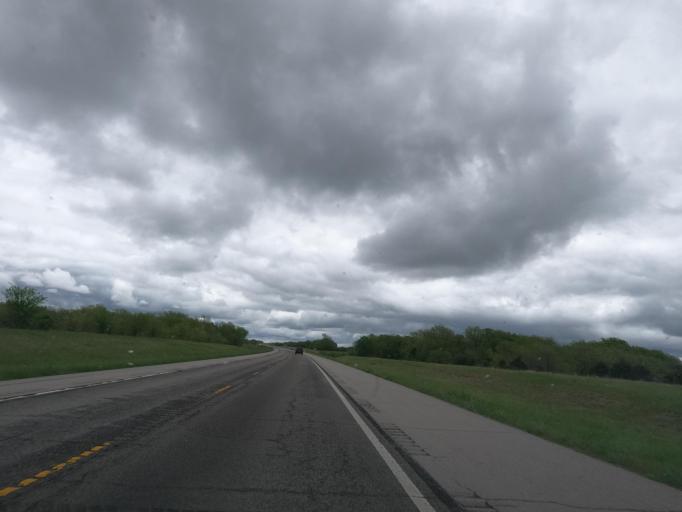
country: US
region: Kansas
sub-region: Montgomery County
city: Cherryvale
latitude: 37.3436
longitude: -95.4544
